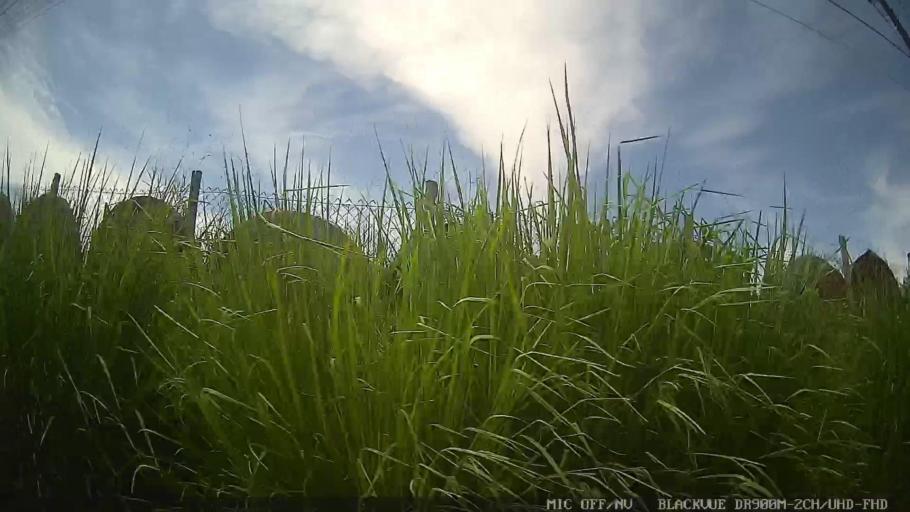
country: BR
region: Sao Paulo
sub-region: Aruja
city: Aruja
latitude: -23.4334
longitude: -46.2575
